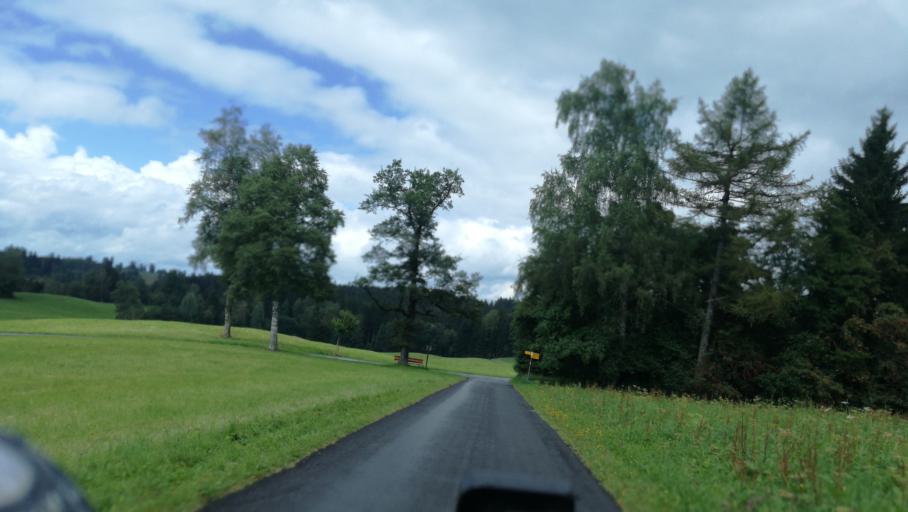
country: CH
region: Zug
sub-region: Zug
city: Walchwil
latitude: 47.1162
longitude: 8.5408
